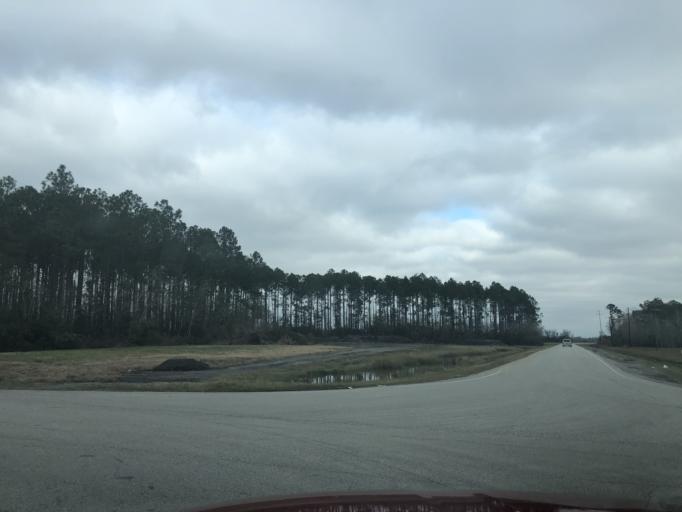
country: US
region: Texas
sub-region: Jefferson County
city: Fannett
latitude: 29.9313
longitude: -94.2654
